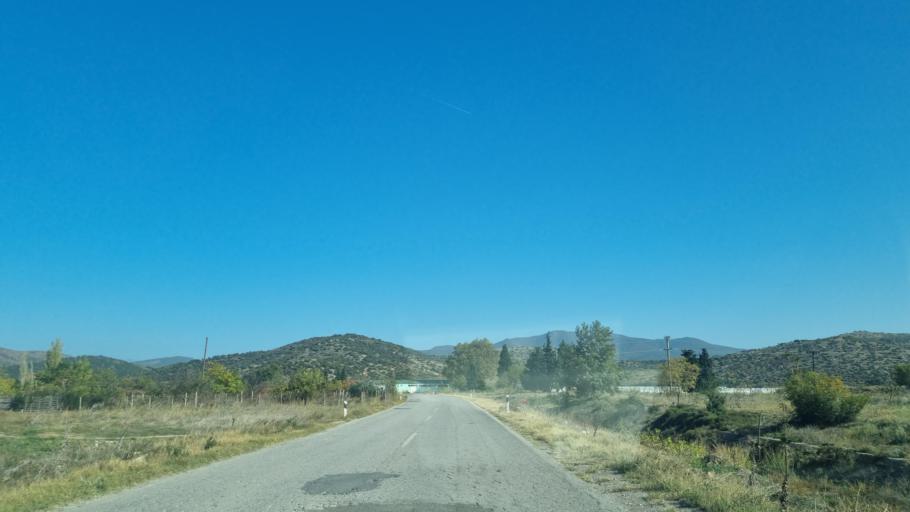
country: MK
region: Bogdanci
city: Bogdanci
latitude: 41.1963
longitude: 22.5803
